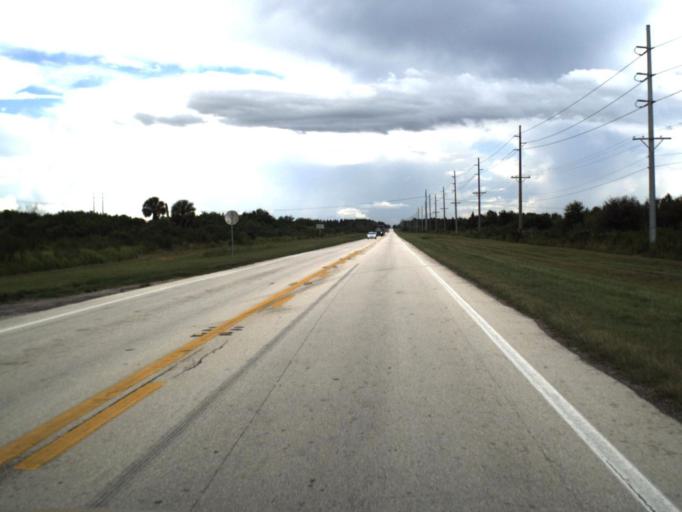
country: US
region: Florida
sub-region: Polk County
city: Mulberry
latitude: 27.8000
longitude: -81.9818
